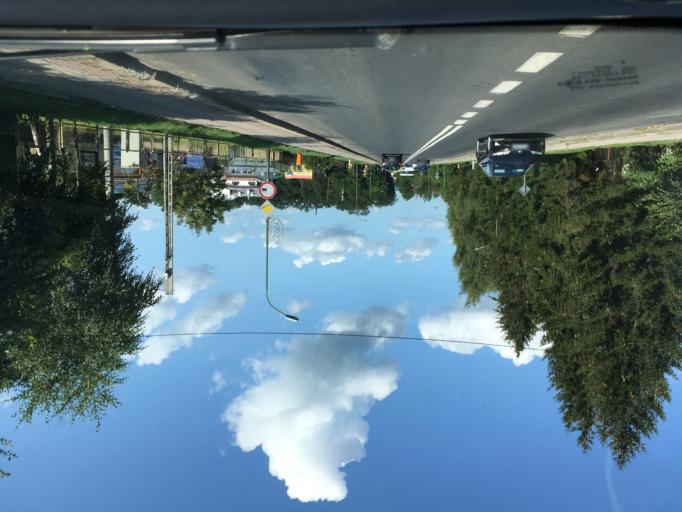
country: PL
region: Subcarpathian Voivodeship
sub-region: Powiat leski
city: Lesko
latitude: 49.4745
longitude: 22.3252
